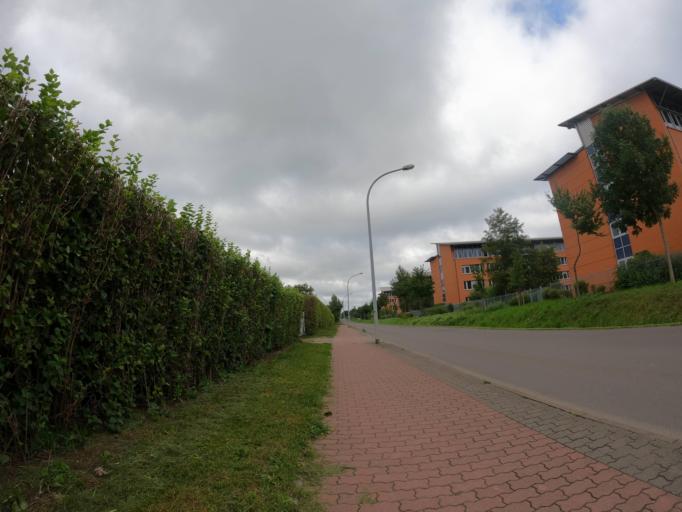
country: DE
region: Mecklenburg-Vorpommern
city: Kramerhof
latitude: 54.3377
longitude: 13.0655
